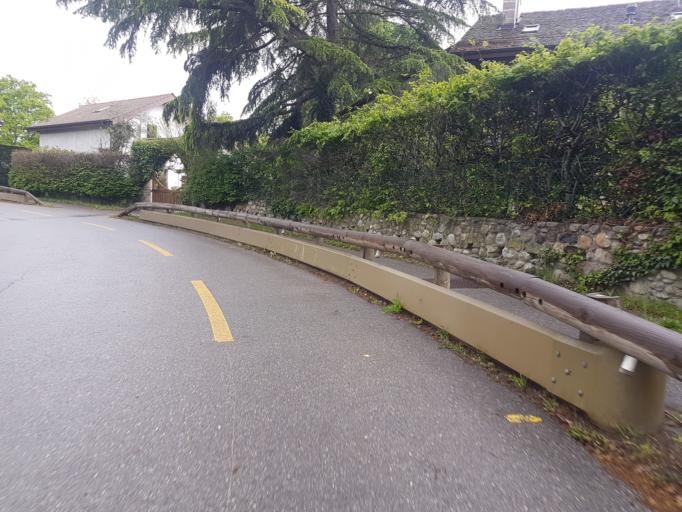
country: CH
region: Geneva
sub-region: Geneva
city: Dardagny
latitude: 46.1756
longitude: 5.9978
